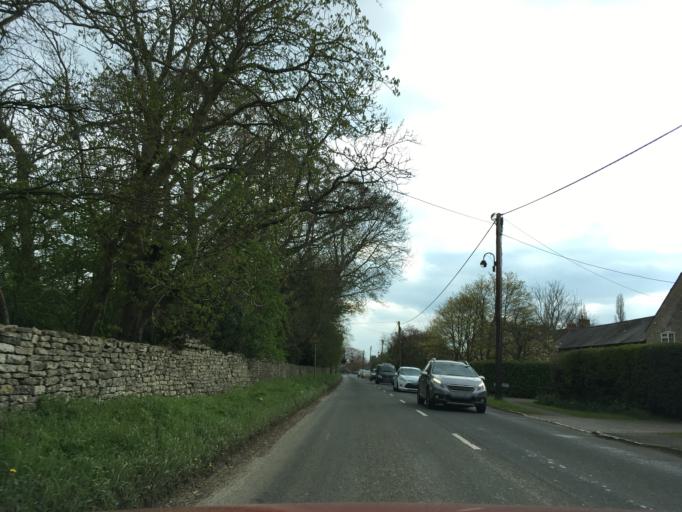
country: GB
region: England
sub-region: Oxfordshire
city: Kidlington
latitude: 51.8786
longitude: -1.2741
